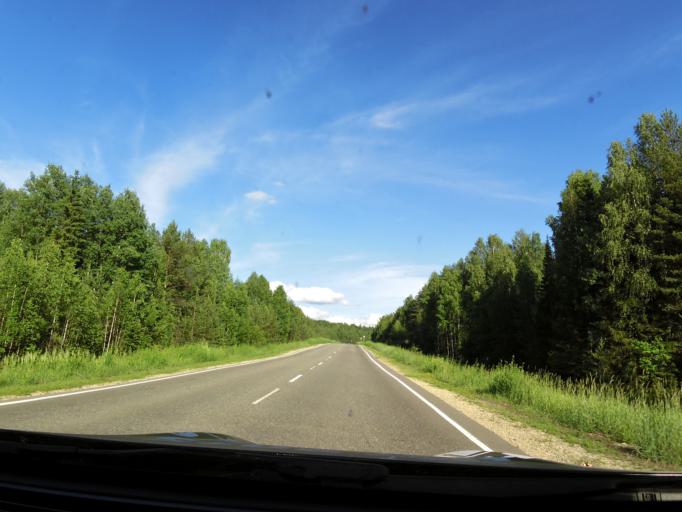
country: RU
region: Kirov
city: Chernaya Kholunitsa
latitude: 58.8229
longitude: 51.7996
